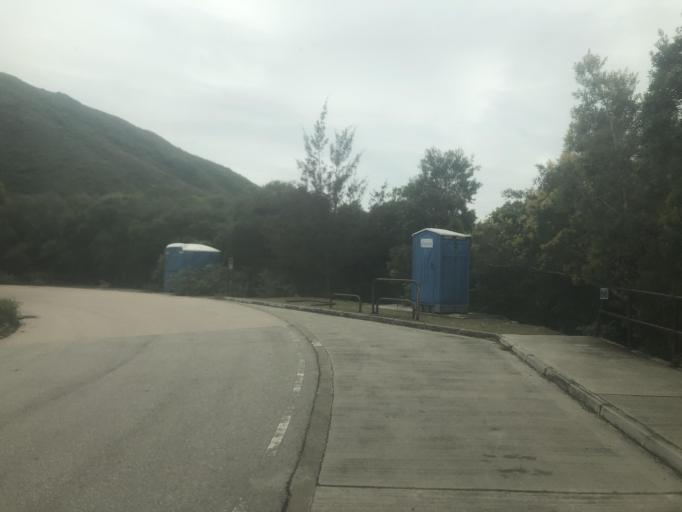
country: HK
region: Sai Kung
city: Sai Kung
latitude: 22.3618
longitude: 114.3712
